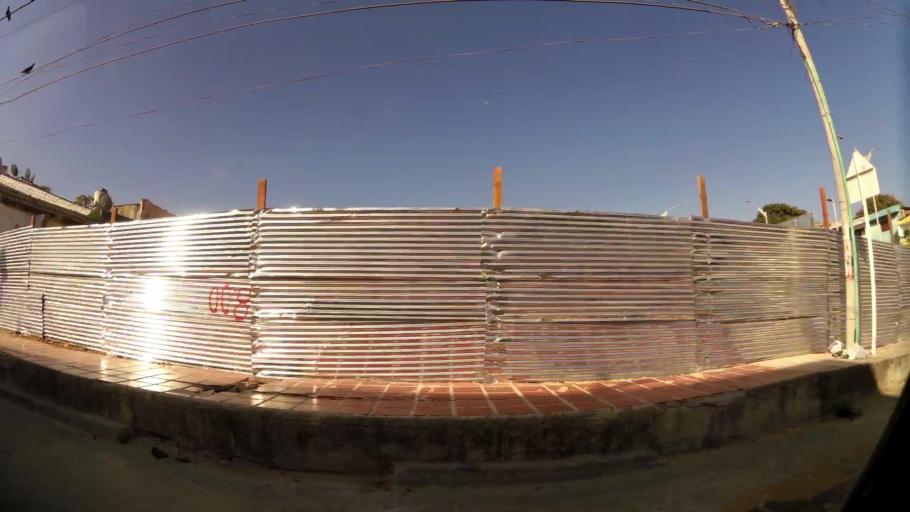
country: CO
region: Atlantico
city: Barranquilla
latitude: 10.9930
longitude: -74.7872
